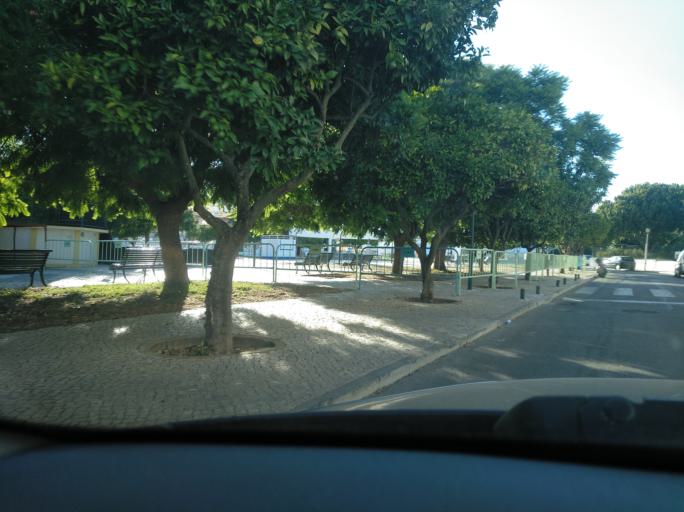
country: PT
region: Faro
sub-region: Vila Real de Santo Antonio
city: Monte Gordo
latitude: 37.1753
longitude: -7.5349
